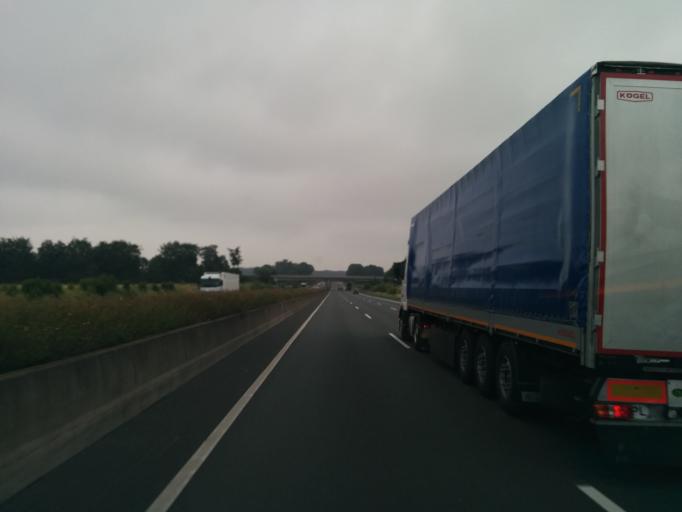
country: DE
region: North Rhine-Westphalia
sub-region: Regierungsbezirk Munster
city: Beckum
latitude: 51.7573
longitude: 8.0001
